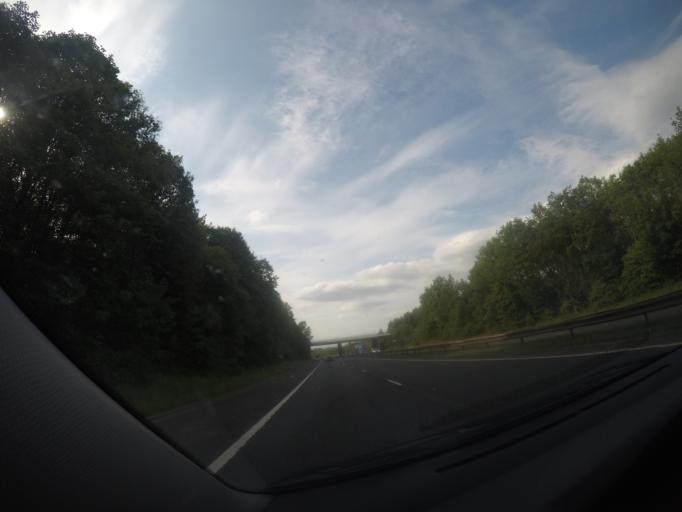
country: GB
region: Scotland
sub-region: South Lanarkshire
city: Larkhall
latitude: 55.7521
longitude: -3.9683
